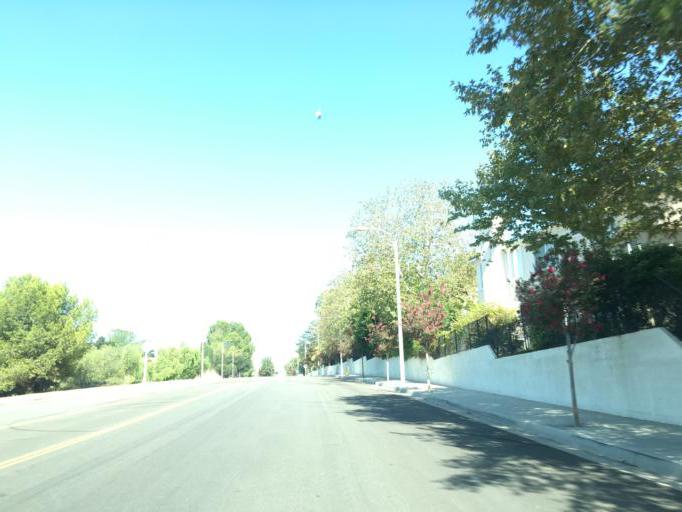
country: US
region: California
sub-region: Los Angeles County
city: Woodland Hills
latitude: 34.1336
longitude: -118.5925
